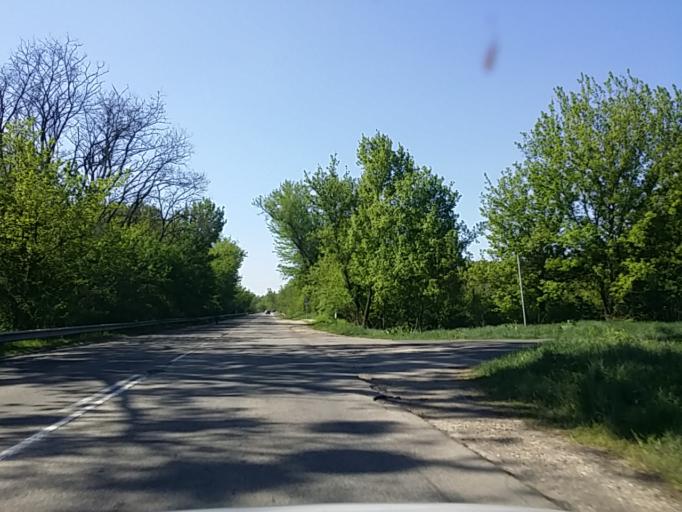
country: HU
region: Pest
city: Godollo
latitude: 47.6006
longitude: 19.4034
